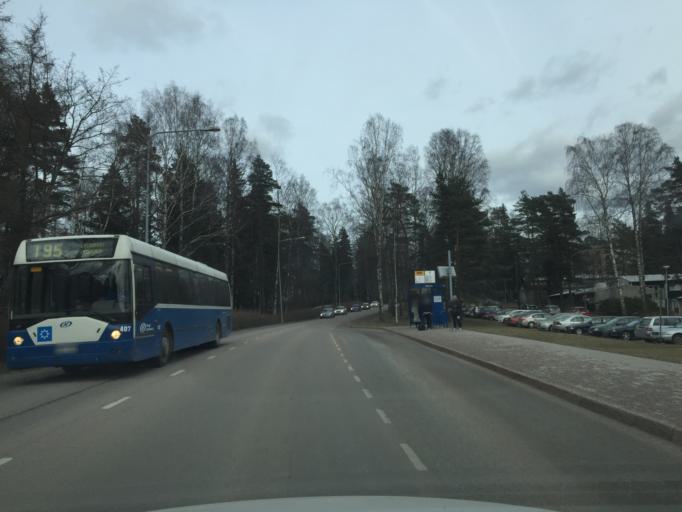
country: FI
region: Uusimaa
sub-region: Helsinki
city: Otaniemi
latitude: 60.1778
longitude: 24.8121
